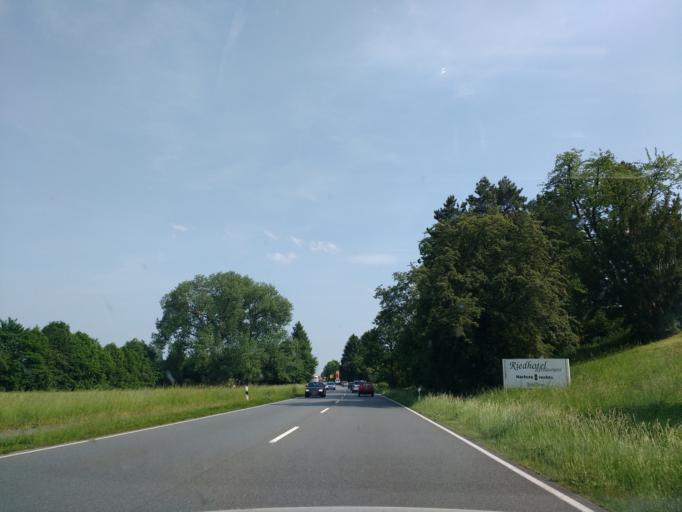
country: DE
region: North Rhine-Westphalia
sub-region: Regierungsbezirk Detmold
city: Bad Salzuflen
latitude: 52.0825
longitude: 8.7171
